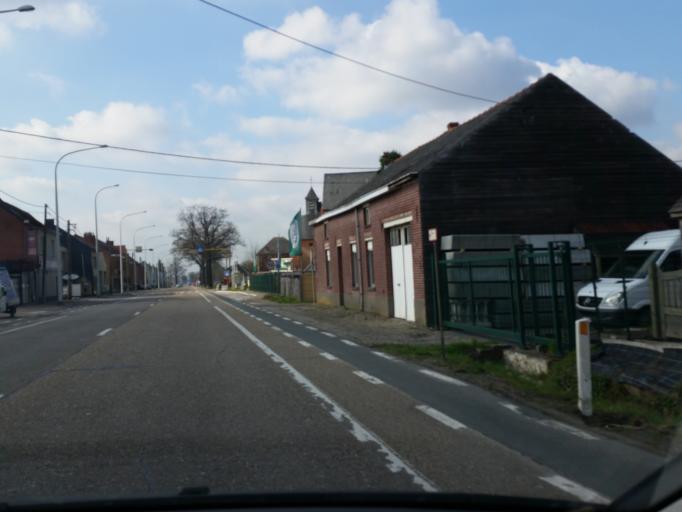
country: BE
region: Flanders
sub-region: Provincie Vlaams-Brabant
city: Herent
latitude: 50.9270
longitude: 4.6377
